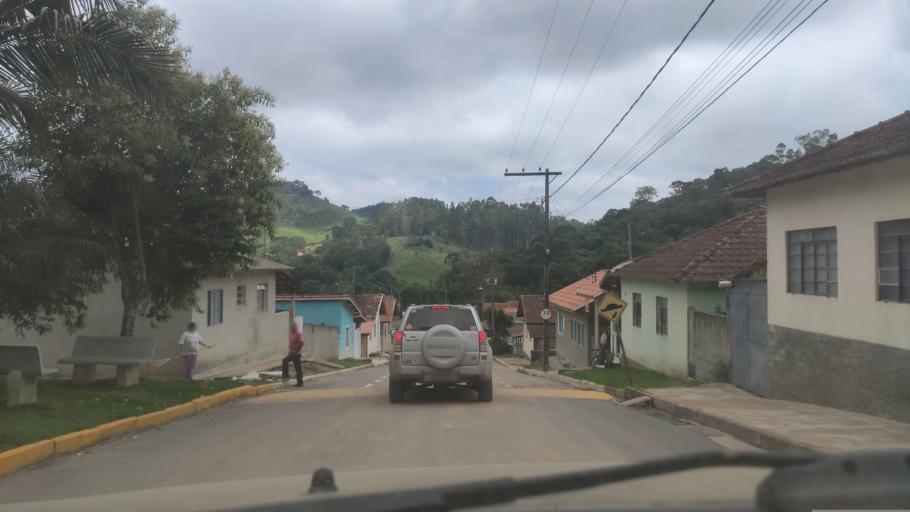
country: BR
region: Minas Gerais
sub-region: Cambui
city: Cambui
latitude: -22.6606
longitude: -45.9153
